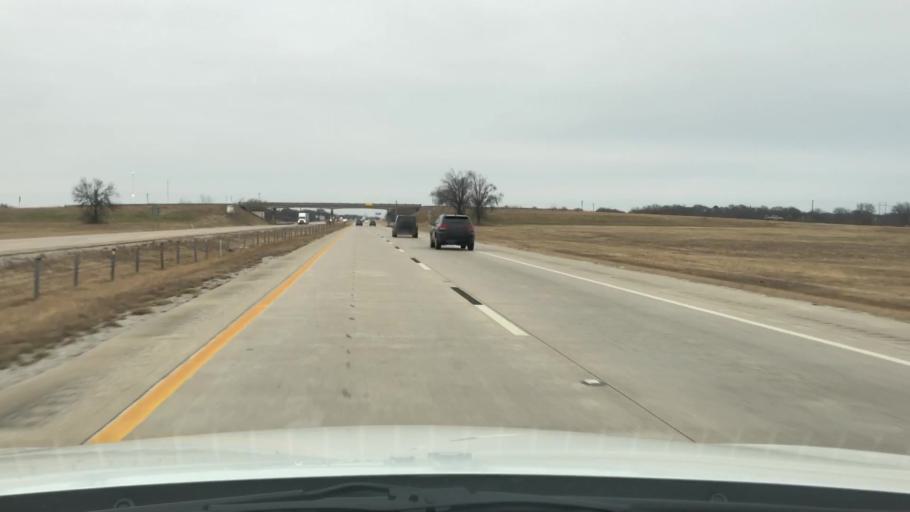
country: US
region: Oklahoma
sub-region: Love County
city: Marietta
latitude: 33.7930
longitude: -97.1348
